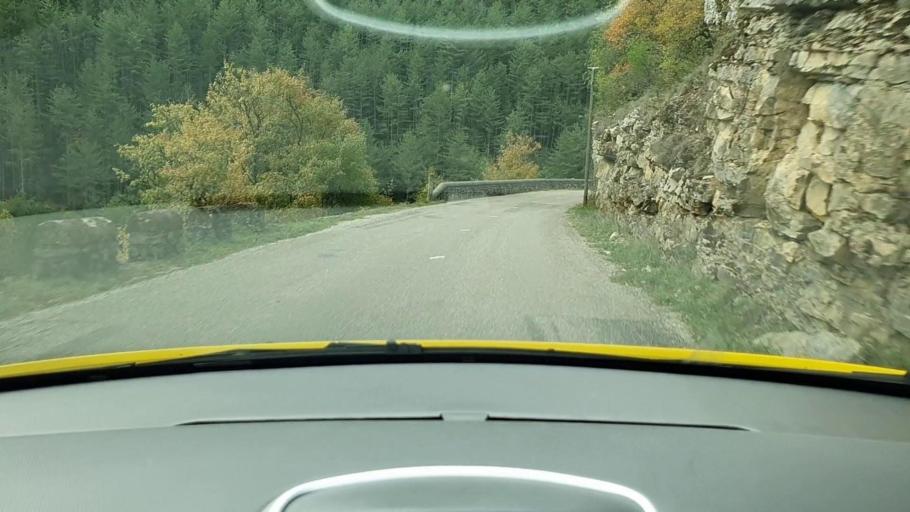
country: FR
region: Languedoc-Roussillon
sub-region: Departement de la Lozere
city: Meyrueis
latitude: 44.0780
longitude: 3.3759
